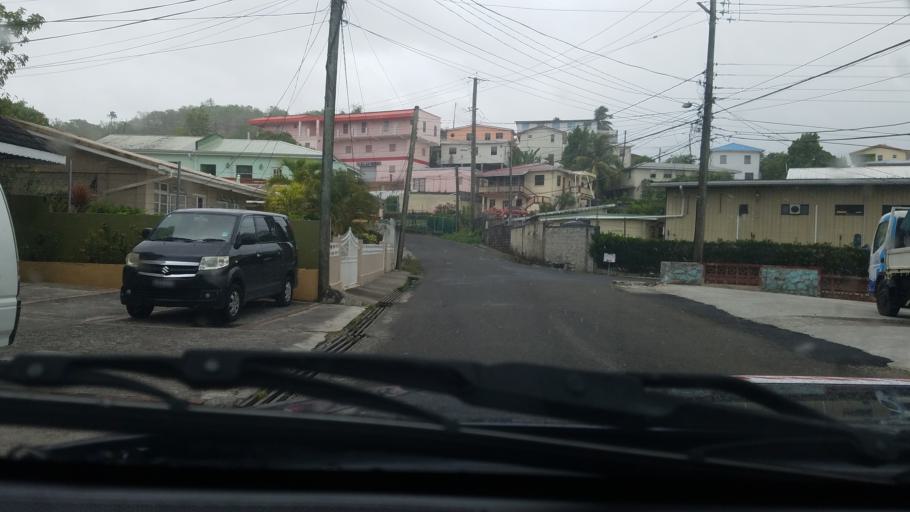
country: LC
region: Castries Quarter
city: Bisee
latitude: 14.0177
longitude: -60.9885
